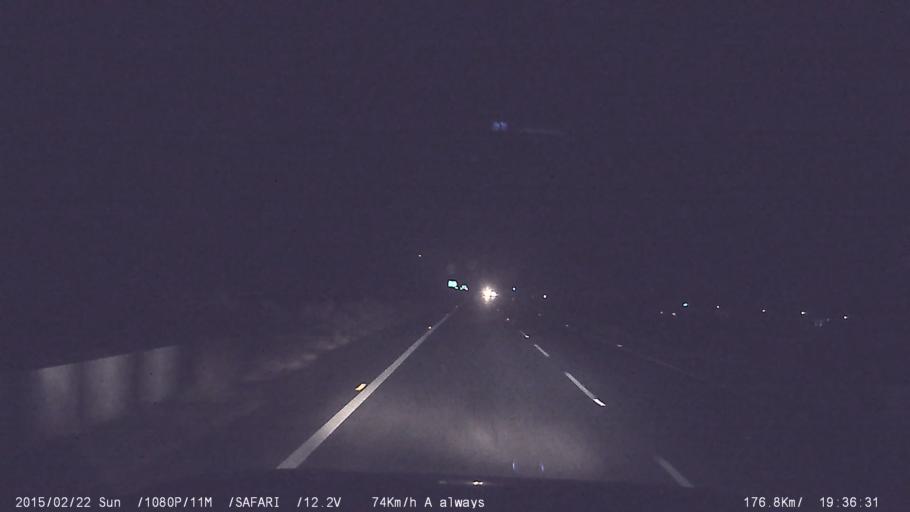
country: IN
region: Tamil Nadu
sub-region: Theni
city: Devadanappatti
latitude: 10.1311
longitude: 77.6154
